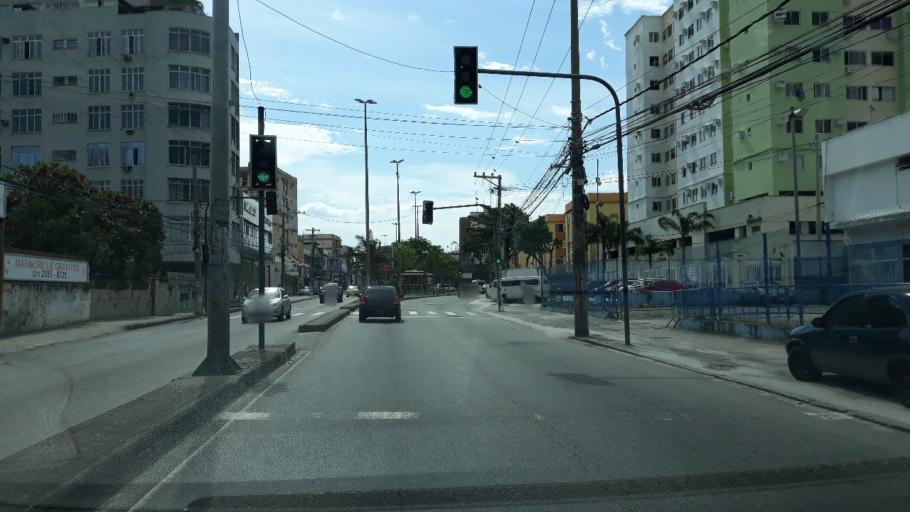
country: BR
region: Rio de Janeiro
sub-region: Duque De Caxias
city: Duque de Caxias
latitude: -22.8849
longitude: -43.3139
